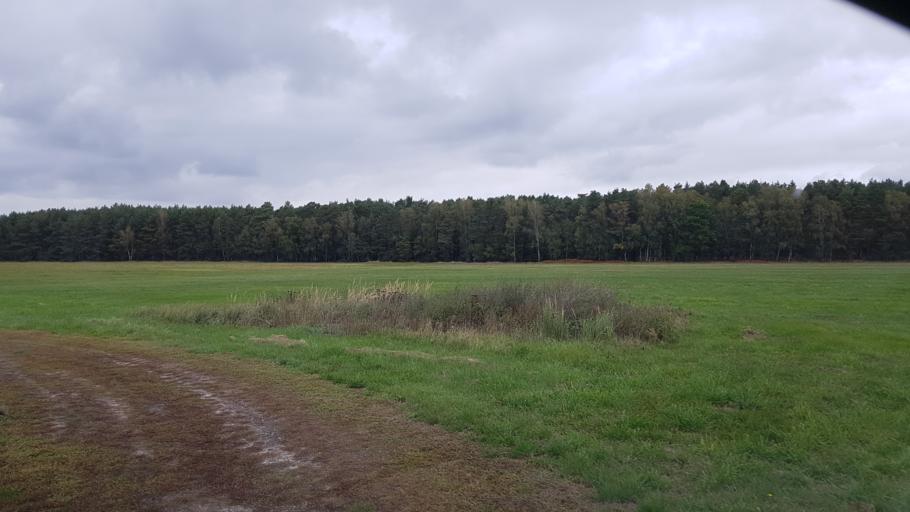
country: DE
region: Brandenburg
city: Finsterwalde
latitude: 51.5790
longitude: 13.6728
